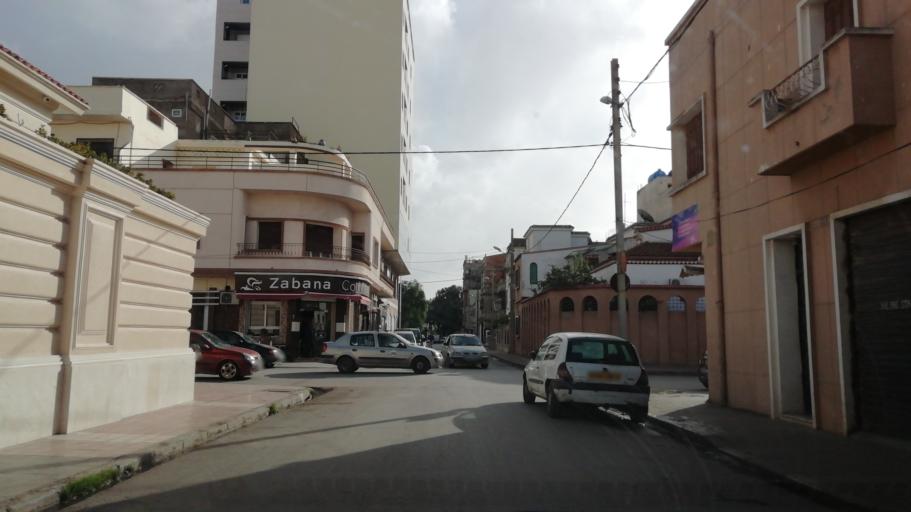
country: DZ
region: Oran
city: Oran
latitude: 35.6953
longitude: -0.6217
